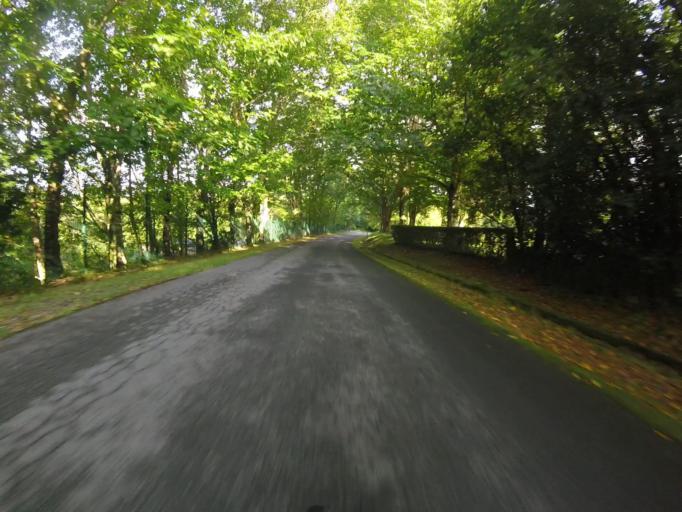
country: ES
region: Basque Country
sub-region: Provincia de Guipuzcoa
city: Irun
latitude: 43.3424
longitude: -1.8353
